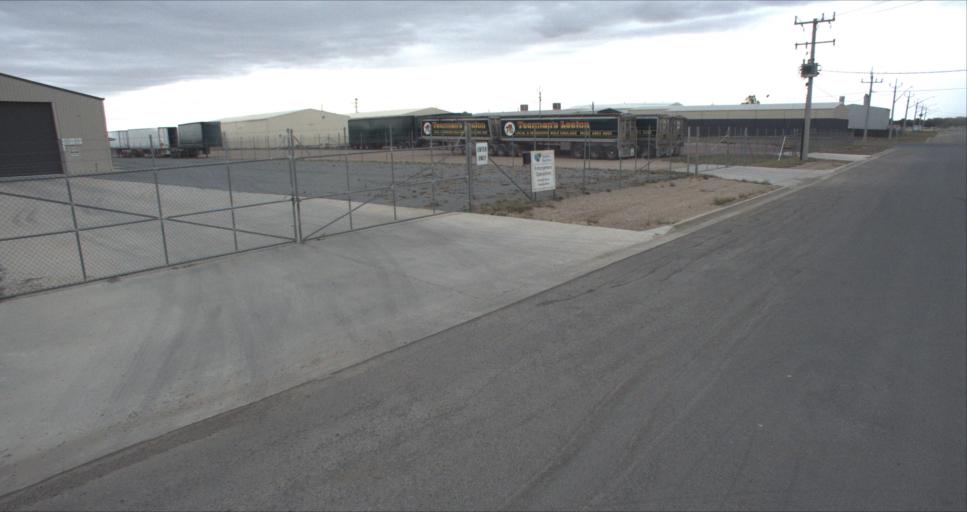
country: AU
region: New South Wales
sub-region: Leeton
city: Leeton
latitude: -34.5469
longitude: 146.3876
